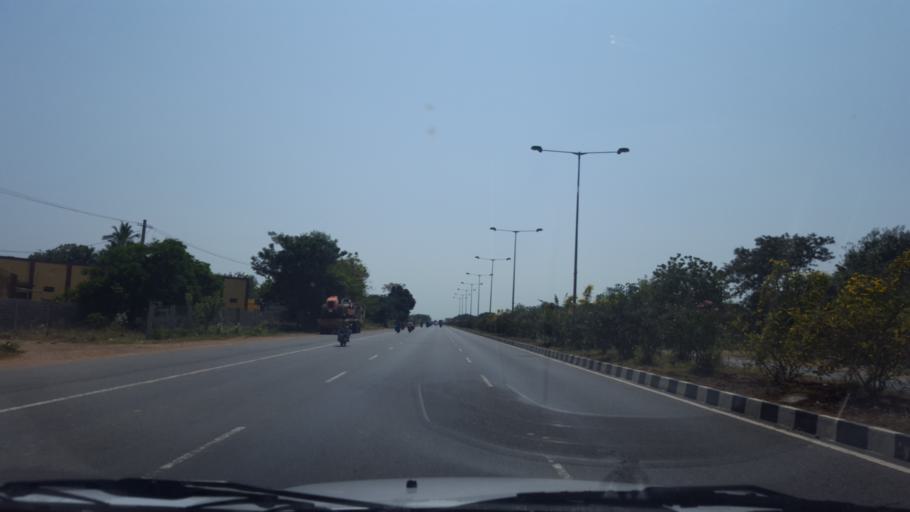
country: IN
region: Andhra Pradesh
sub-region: Prakasam
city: Ongole
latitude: 15.6009
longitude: 80.0305
